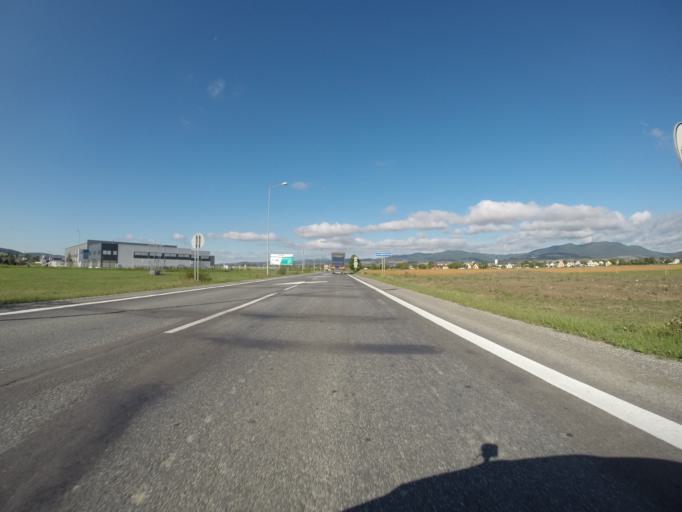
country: SK
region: Trenciansky
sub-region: Okres Trencin
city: Trencin
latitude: 48.8485
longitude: 17.9913
